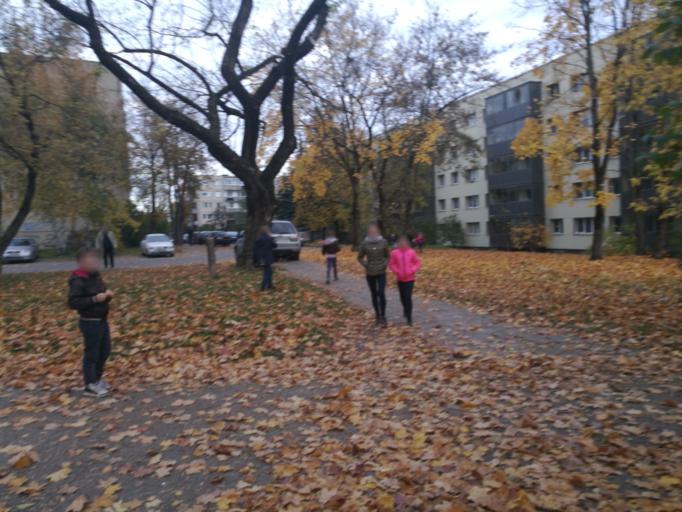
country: LT
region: Vilnius County
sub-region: Vilnius
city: Vilnius
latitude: 54.7007
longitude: 25.3000
